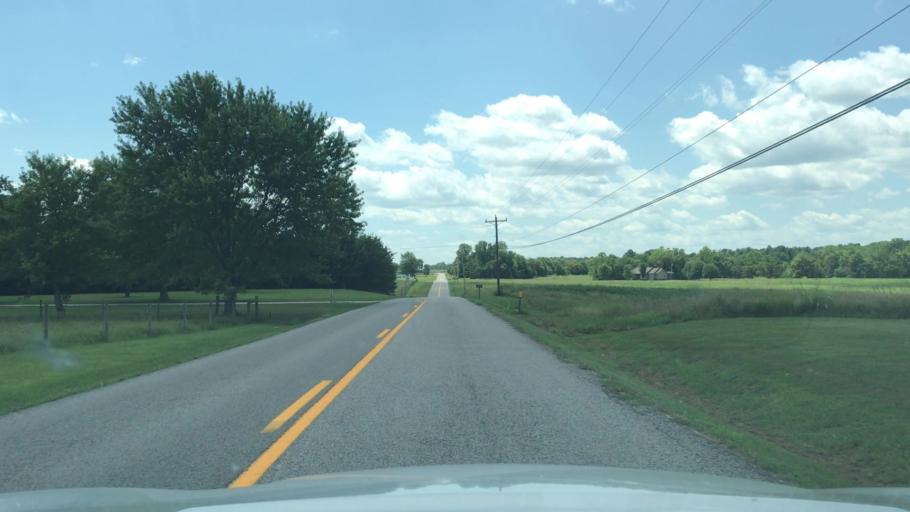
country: US
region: Kentucky
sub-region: Christian County
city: Hopkinsville
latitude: 36.9665
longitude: -87.3850
